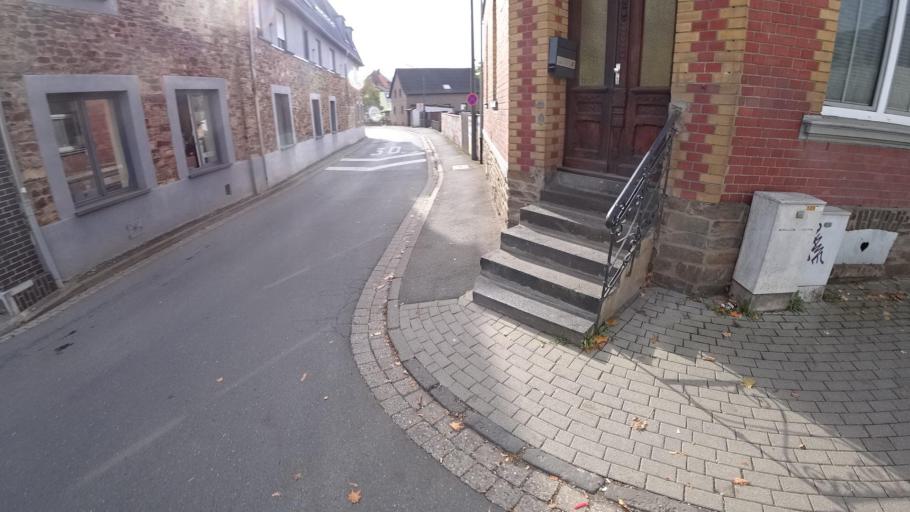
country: DE
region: Rheinland-Pfalz
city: Bad Neuenahr-Ahrweiler
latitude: 50.5457
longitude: 7.1048
